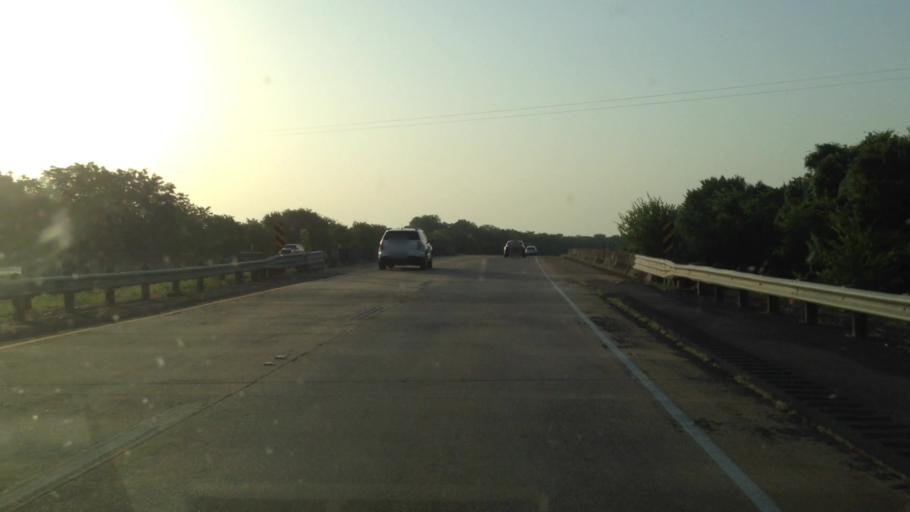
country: US
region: Louisiana
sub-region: Natchitoches Parish
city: Vienna Bend
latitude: 31.5684
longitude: -92.9966
